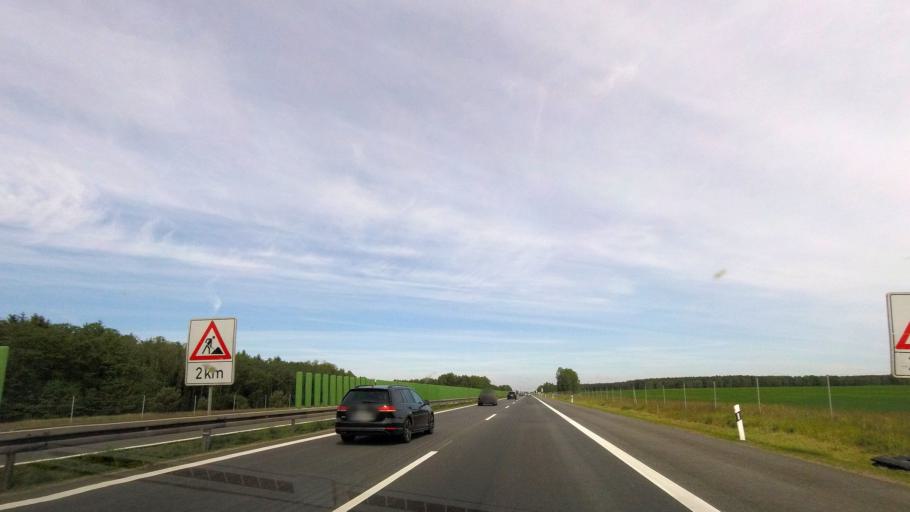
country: DE
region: Brandenburg
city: Walsleben
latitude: 52.9938
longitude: 12.6083
